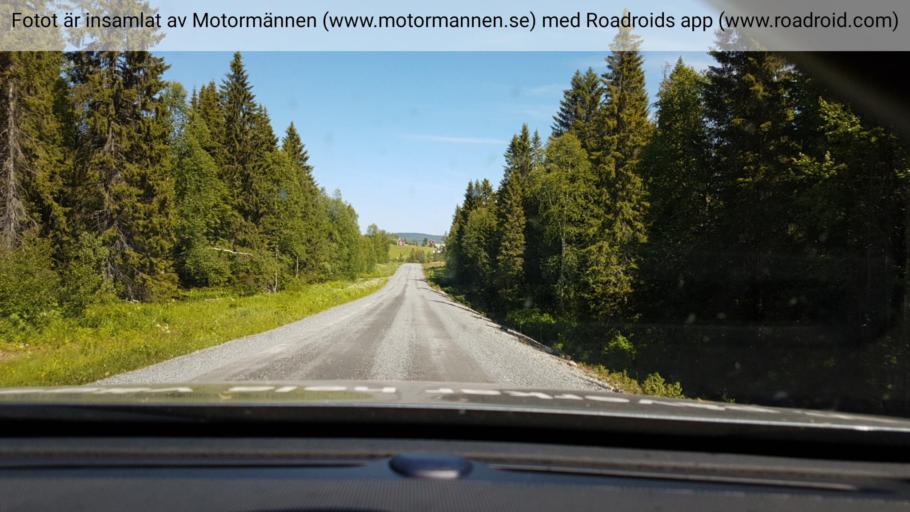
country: SE
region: Vaesterbotten
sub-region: Vilhelmina Kommun
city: Sjoberg
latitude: 64.7822
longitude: 15.9552
